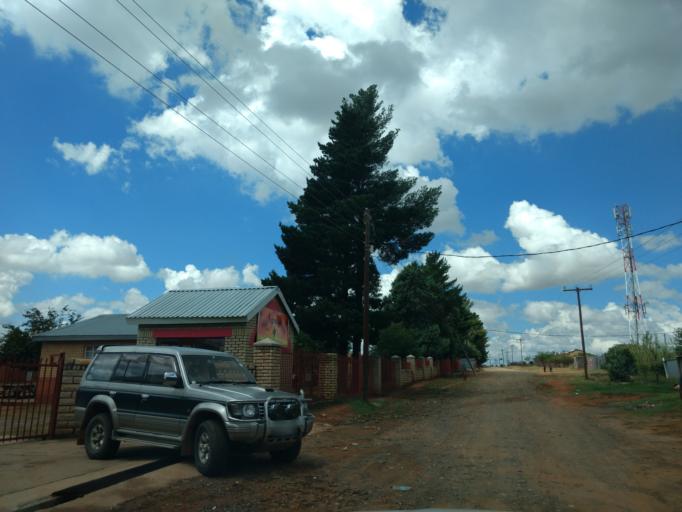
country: LS
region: Maseru
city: Maseru
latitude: -29.3723
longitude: 27.5062
